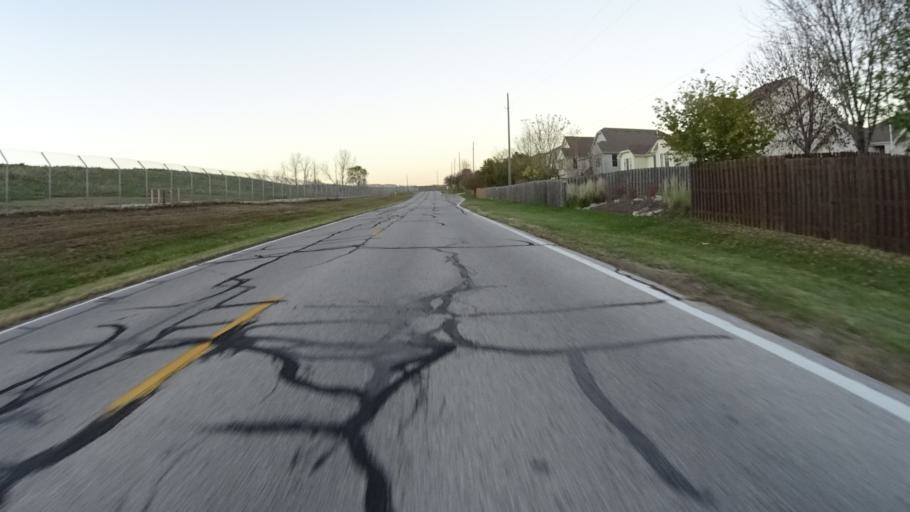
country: US
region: Nebraska
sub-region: Sarpy County
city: Offutt Air Force Base
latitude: 41.1635
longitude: -95.9560
